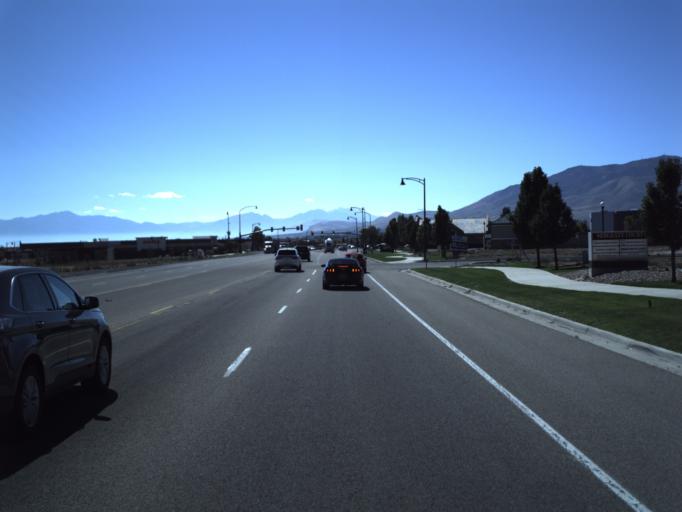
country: US
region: Utah
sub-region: Utah County
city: Saratoga Springs
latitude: 40.3929
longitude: -111.9175
